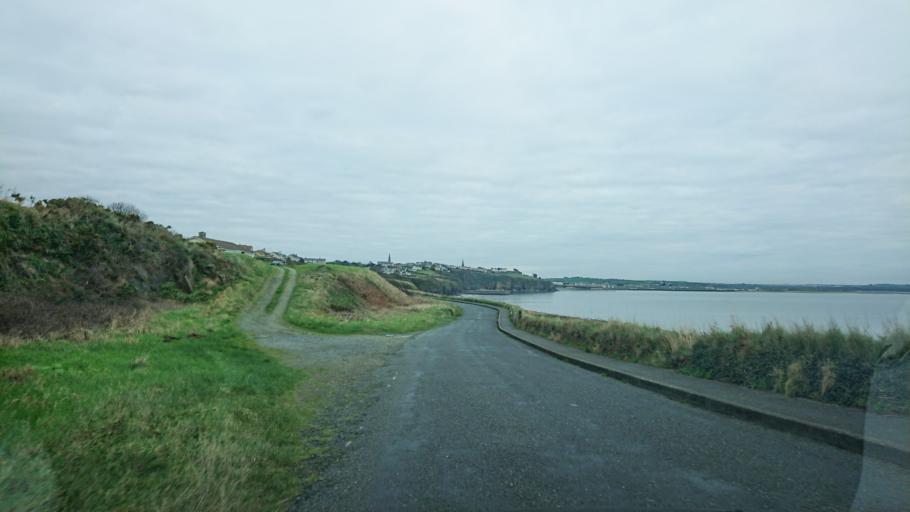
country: IE
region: Munster
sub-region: Waterford
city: Tra Mhor
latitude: 52.1455
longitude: -7.1643
